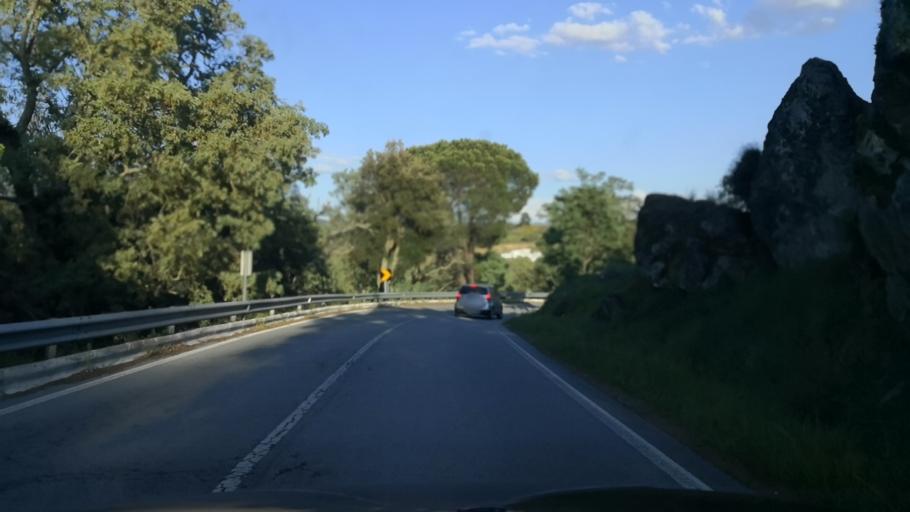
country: PT
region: Portalegre
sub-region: Marvao
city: Marvao
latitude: 39.3652
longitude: -7.3964
